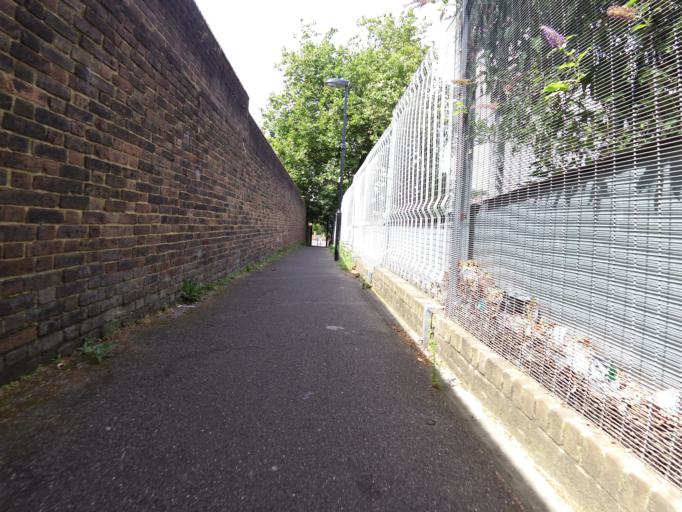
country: GB
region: England
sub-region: Greater London
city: Holloway
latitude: 51.5533
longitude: -0.1306
